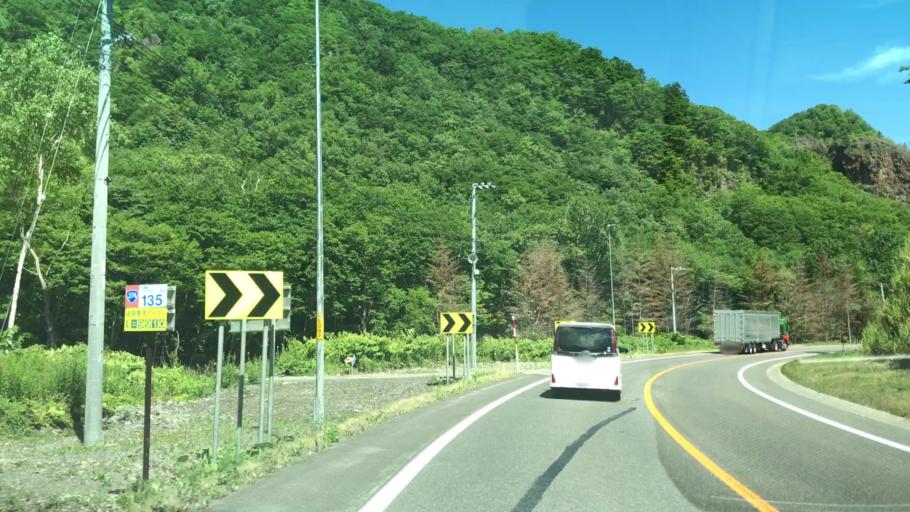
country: JP
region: Hokkaido
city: Shimo-furano
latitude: 42.9174
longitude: 142.5863
